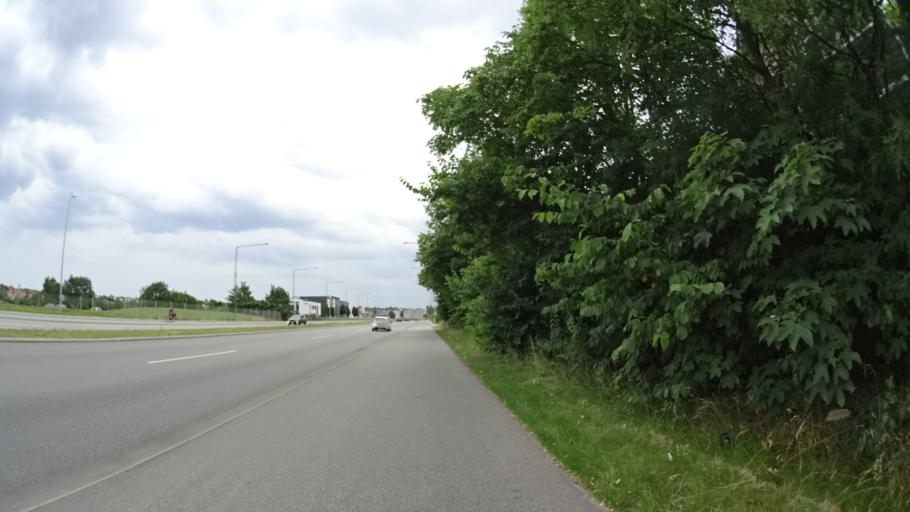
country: DK
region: Central Jutland
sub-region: Arhus Kommune
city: Stavtrup
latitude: 56.1346
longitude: 10.1563
